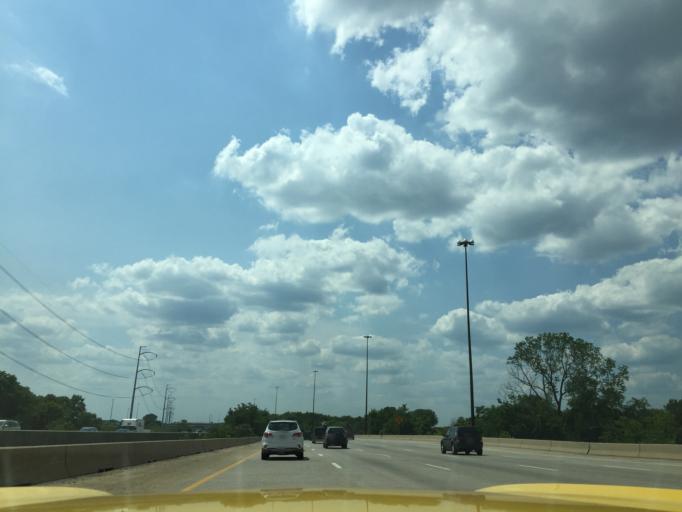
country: US
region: Pennsylvania
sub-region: Delaware County
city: Folcroft
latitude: 39.8764
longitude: -75.2649
